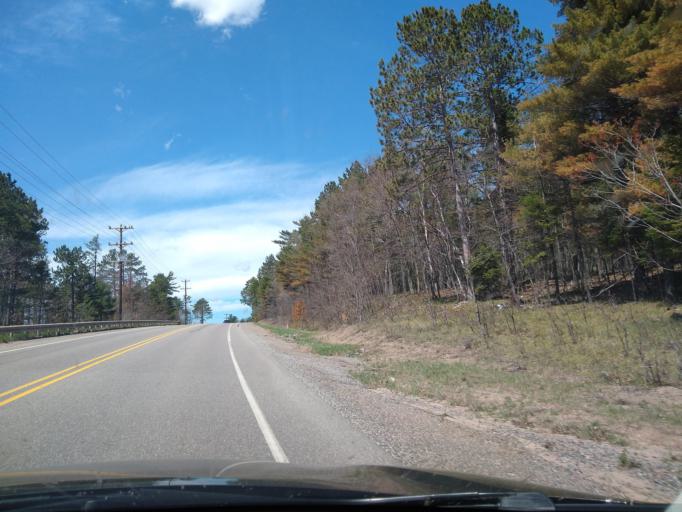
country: US
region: Michigan
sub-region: Marquette County
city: Trowbridge Park
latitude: 46.5913
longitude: -87.4497
